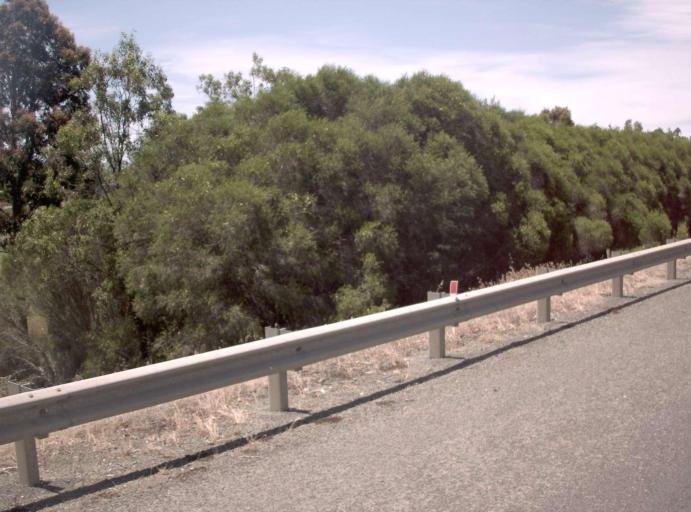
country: AU
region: Victoria
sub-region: Latrobe
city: Morwell
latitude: -38.2414
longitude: 146.4074
